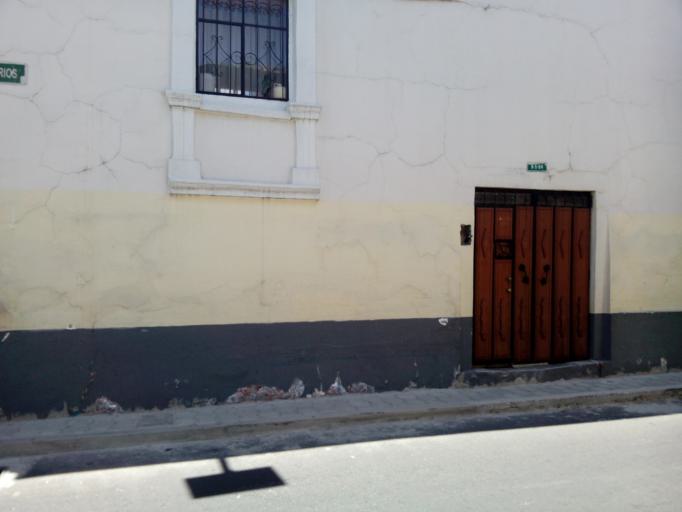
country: EC
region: Pichincha
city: Quito
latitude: -0.2249
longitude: -78.5044
